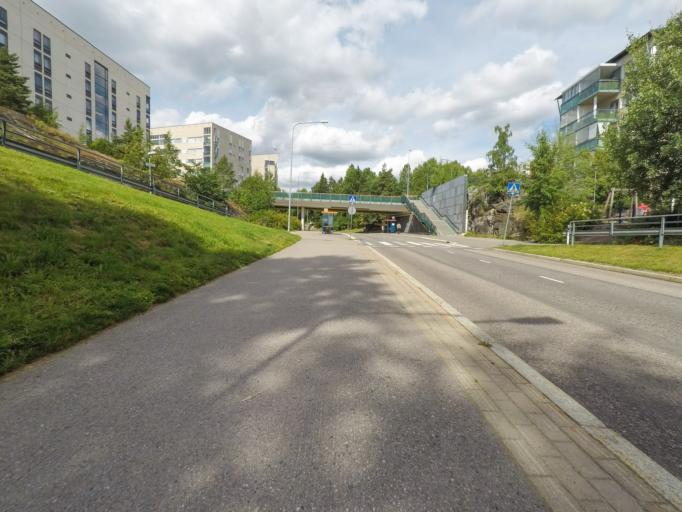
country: FI
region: Uusimaa
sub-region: Helsinki
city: Vantaa
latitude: 60.2297
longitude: 24.9989
